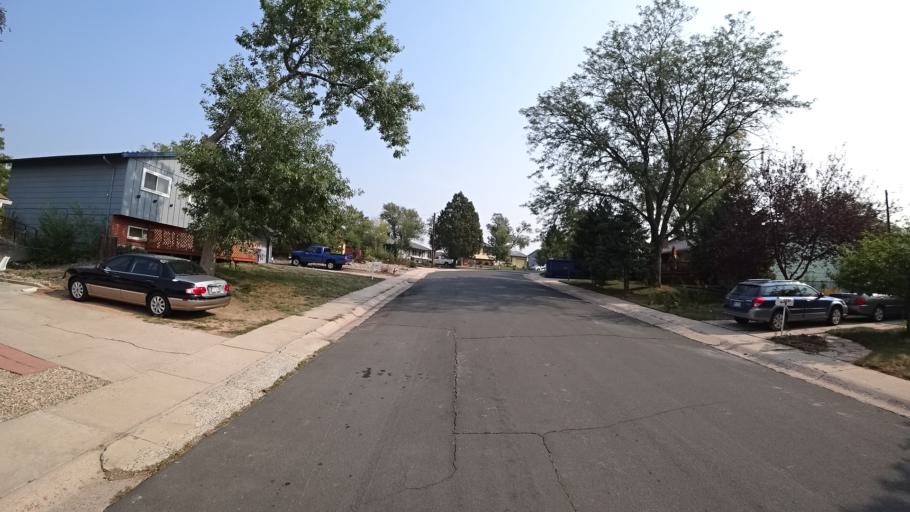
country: US
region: Colorado
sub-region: El Paso County
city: Stratmoor
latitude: 38.8135
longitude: -104.7724
